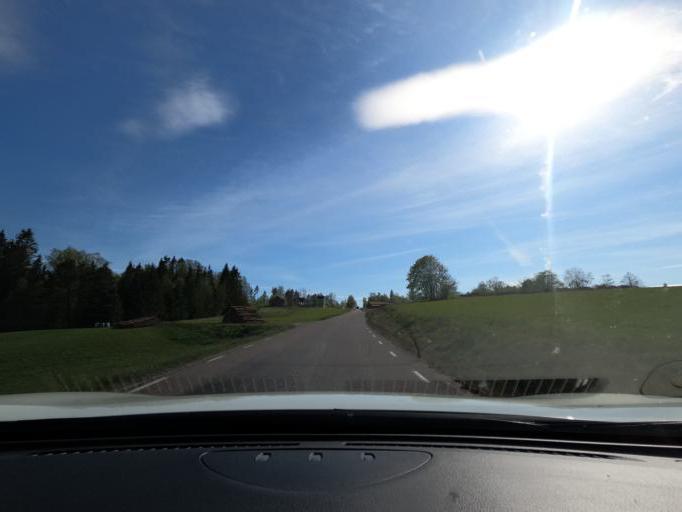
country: SE
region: Vaestra Goetaland
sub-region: Harryda Kommun
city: Landvetter
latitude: 57.6300
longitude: 12.3272
